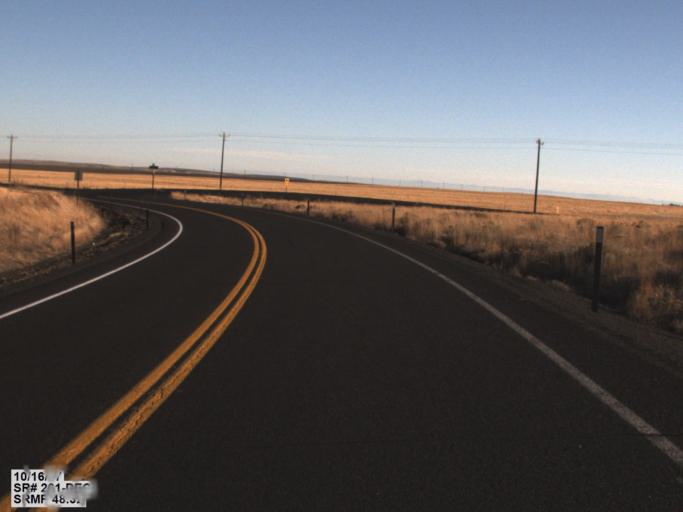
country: US
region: Washington
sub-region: Adams County
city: Ritzville
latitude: 46.9143
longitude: -118.3426
